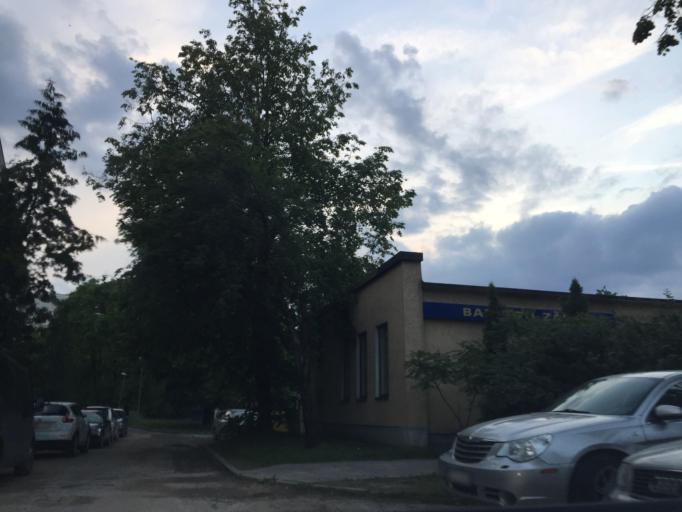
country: LV
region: Riga
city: Riga
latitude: 56.9733
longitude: 24.0628
